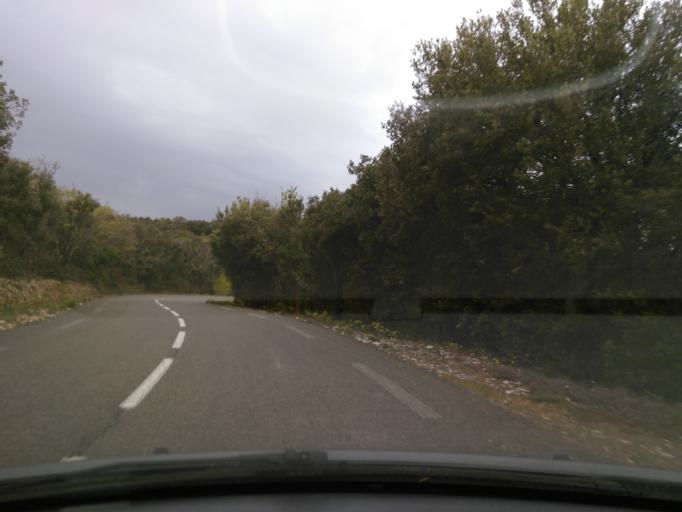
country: FR
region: Languedoc-Roussillon
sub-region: Departement du Gard
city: Barjac
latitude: 44.3287
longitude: 4.4154
